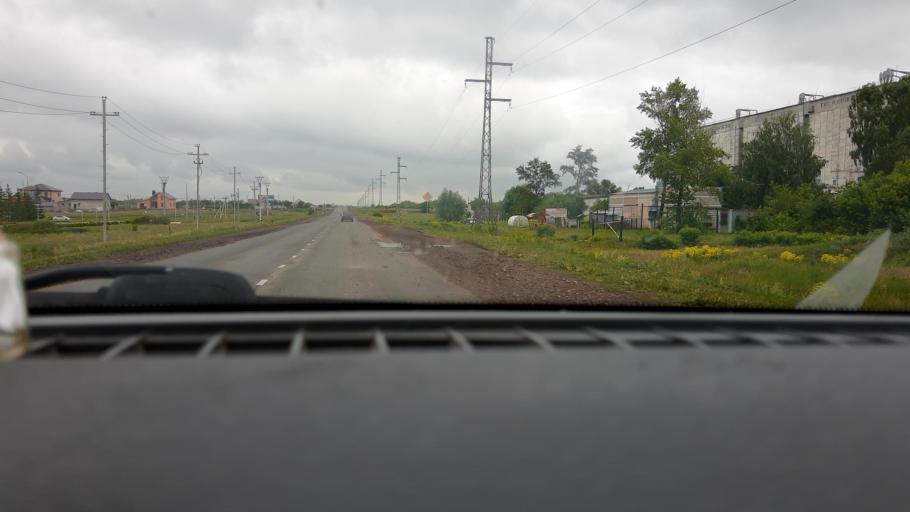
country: RU
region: Bashkortostan
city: Priyutovo
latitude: 53.9061
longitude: 53.9421
